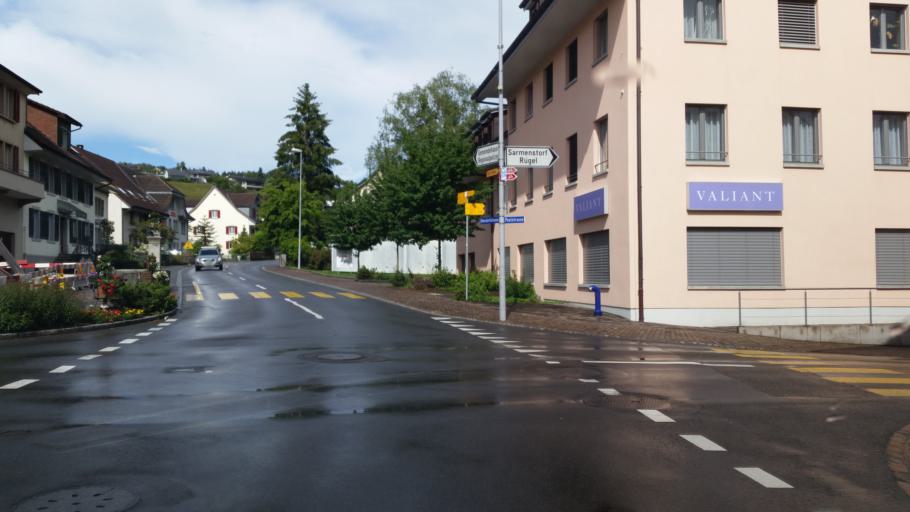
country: CH
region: Aargau
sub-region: Bezirk Lenzburg
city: Seengen
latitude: 47.3268
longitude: 8.2054
